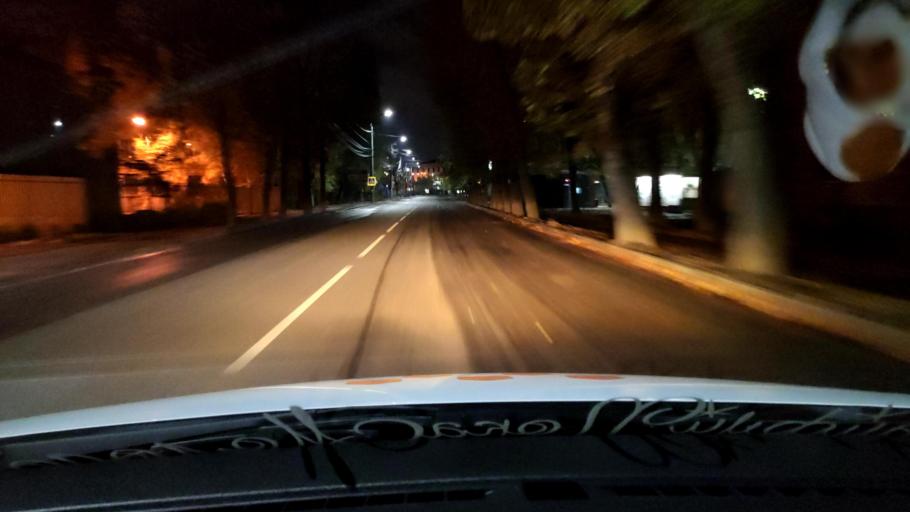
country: RU
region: Voronezj
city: Voronezh
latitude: 51.6858
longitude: 39.1791
